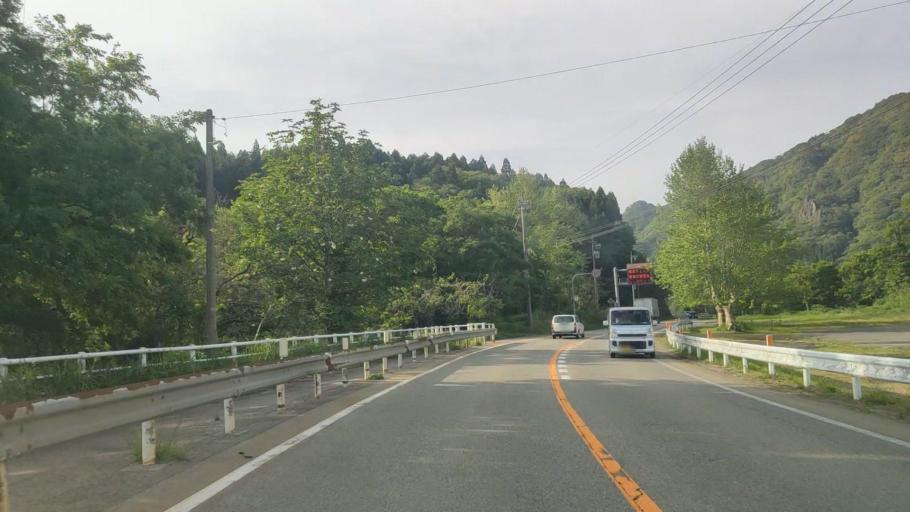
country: JP
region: Toyama
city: Yatsuomachi-higashikumisaka
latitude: 36.5399
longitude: 137.2293
